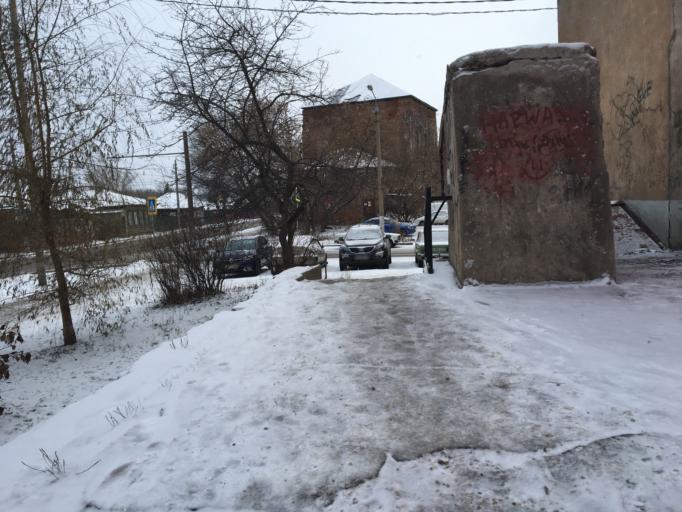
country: RU
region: Tula
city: Tula
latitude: 54.2082
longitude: 37.6066
